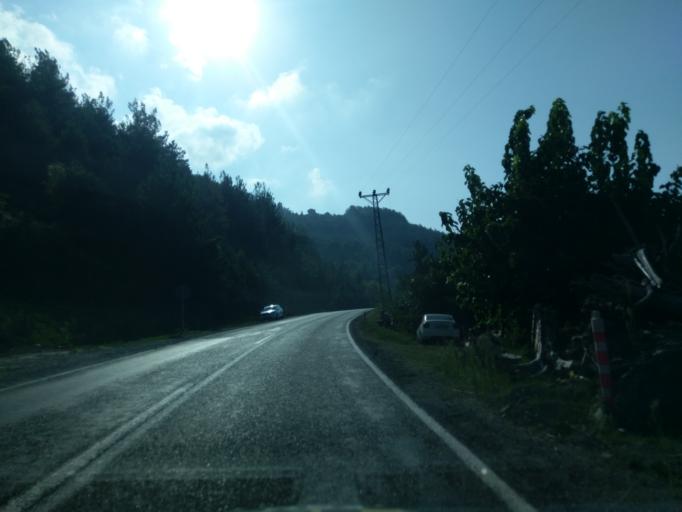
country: TR
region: Sinop
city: Ayancik
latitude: 41.9407
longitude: 34.6501
